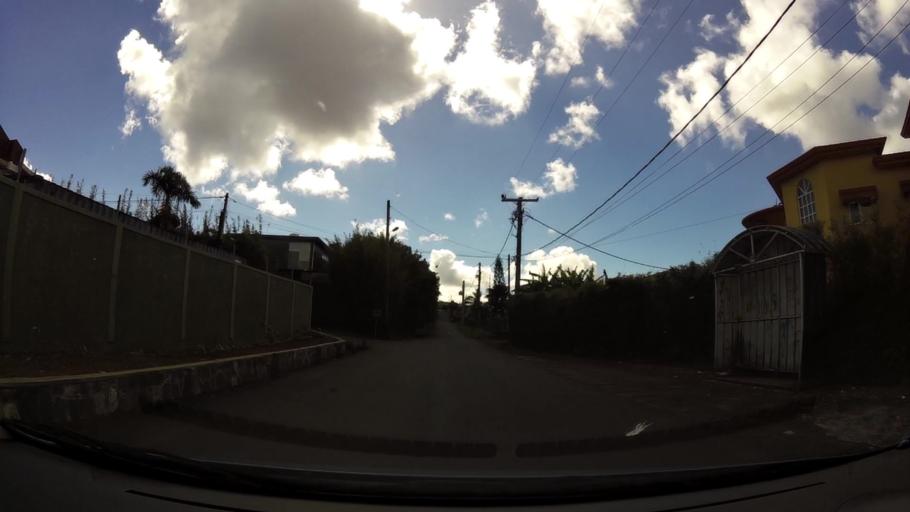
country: MU
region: Plaines Wilhems
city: Curepipe
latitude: -20.3222
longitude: 57.5366
